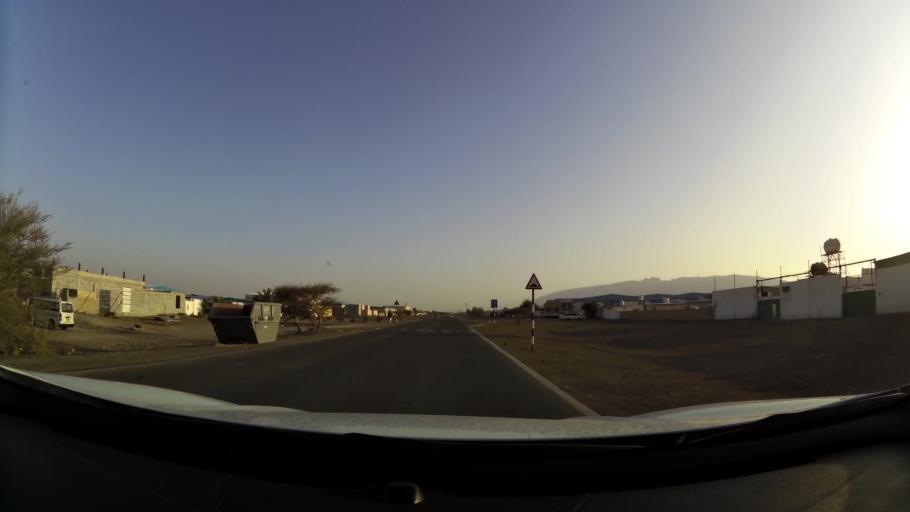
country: AE
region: Abu Dhabi
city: Al Ain
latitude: 24.1532
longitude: 55.8190
